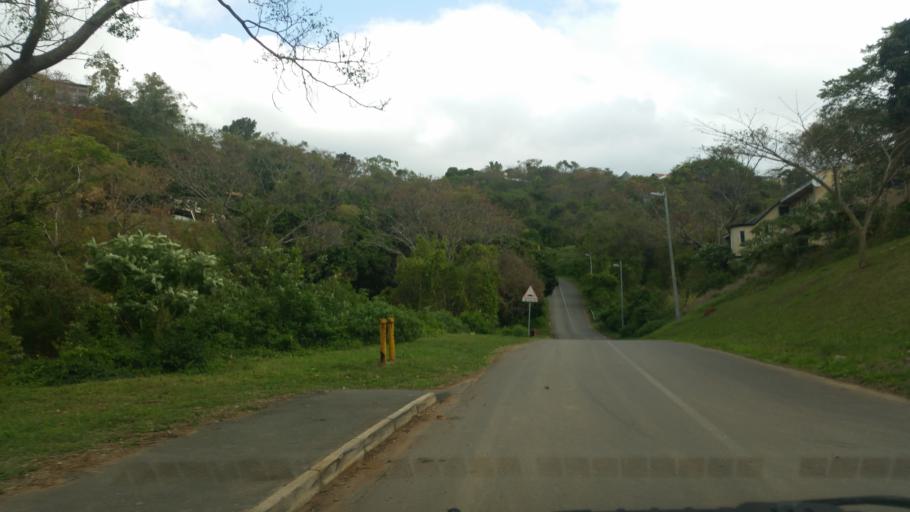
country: ZA
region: KwaZulu-Natal
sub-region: eThekwini Metropolitan Municipality
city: Berea
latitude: -29.8270
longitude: 30.9486
